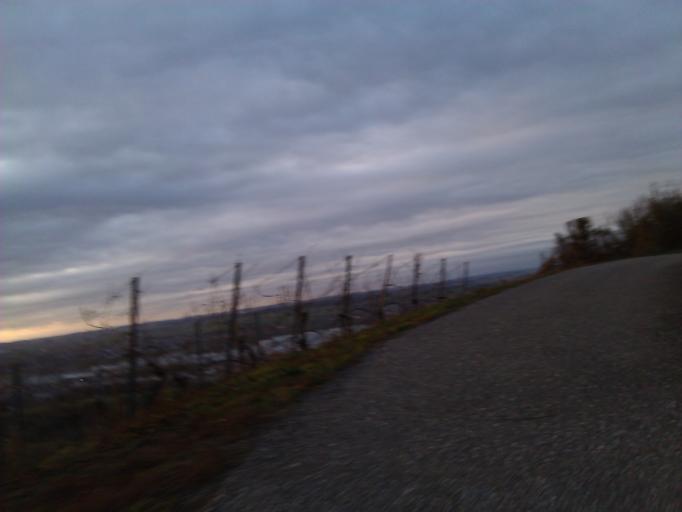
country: DE
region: Baden-Wuerttemberg
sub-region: Regierungsbezirk Stuttgart
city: Neckarsulm
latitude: 49.1957
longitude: 9.2509
